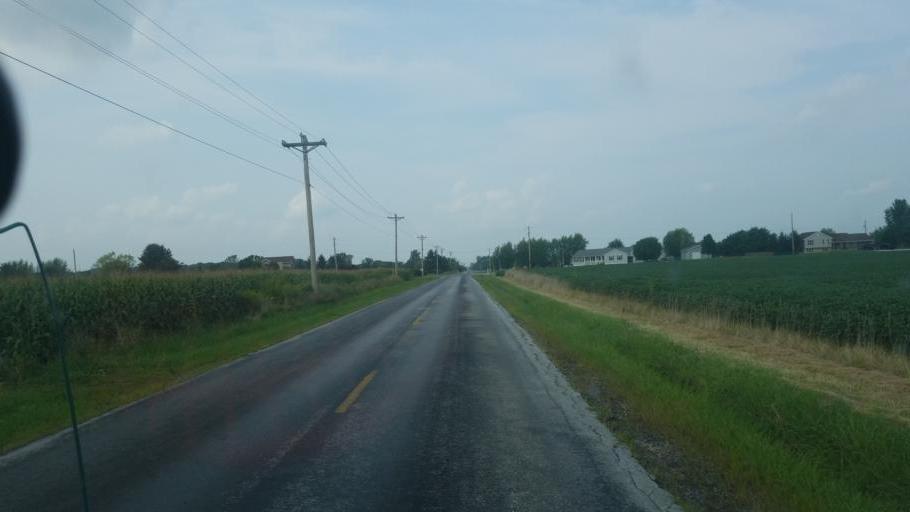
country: US
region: Ohio
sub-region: Lorain County
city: Wellington
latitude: 41.0844
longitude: -82.1617
